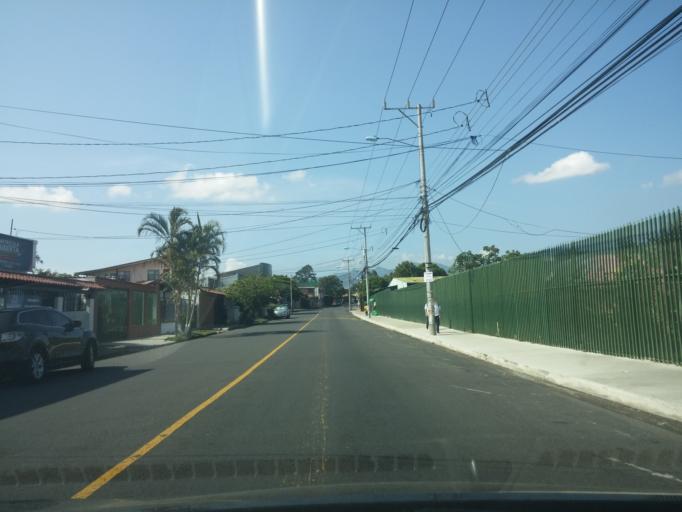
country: CR
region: Heredia
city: San Francisco
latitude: 9.9992
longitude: -84.1285
